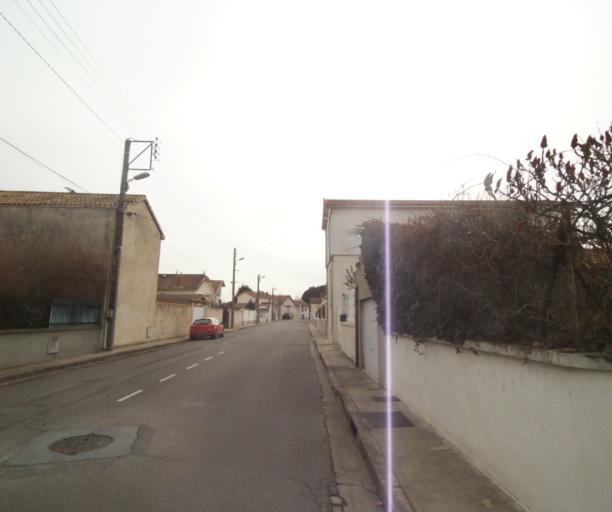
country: FR
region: Rhone-Alpes
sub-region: Departement de la Loire
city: Roanne
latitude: 46.0293
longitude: 4.0600
